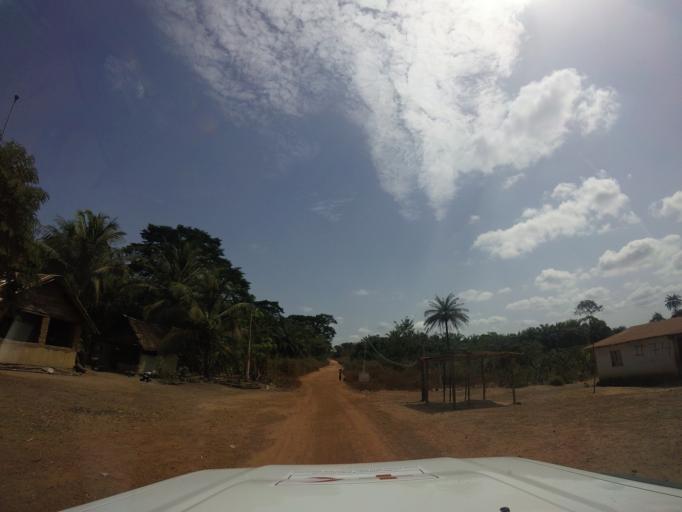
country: LR
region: Grand Cape Mount
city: Robertsport
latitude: 6.9741
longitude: -11.3085
